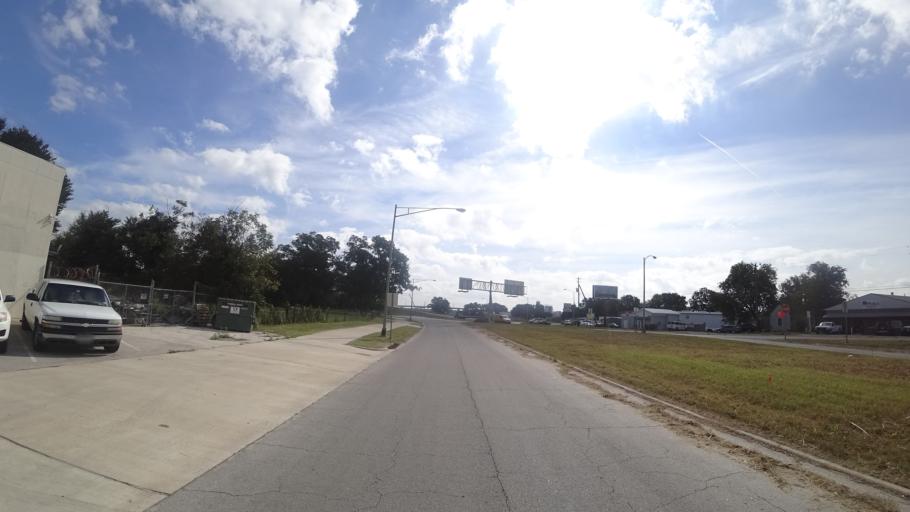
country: US
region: Texas
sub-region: Travis County
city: Austin
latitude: 30.2517
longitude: -97.6973
